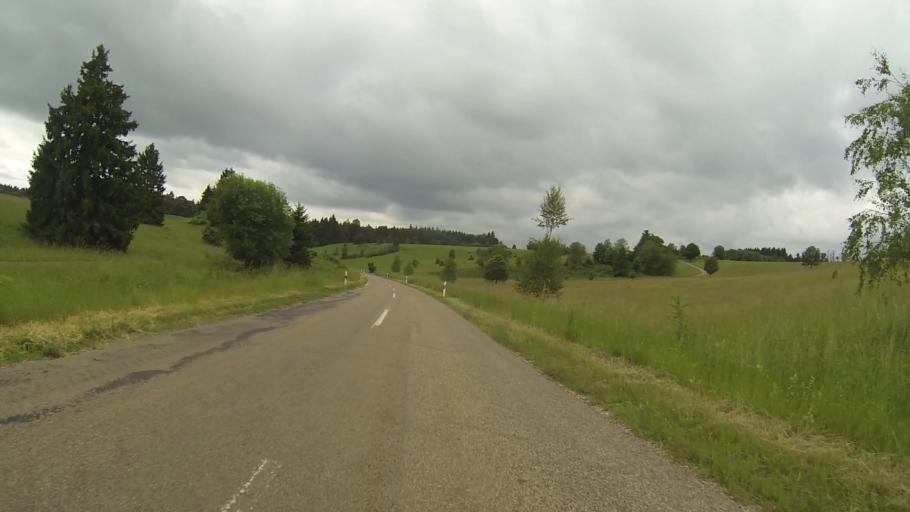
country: DE
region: Baden-Wuerttemberg
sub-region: Regierungsbezirk Stuttgart
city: Gerstetten
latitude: 48.6859
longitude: 9.9982
